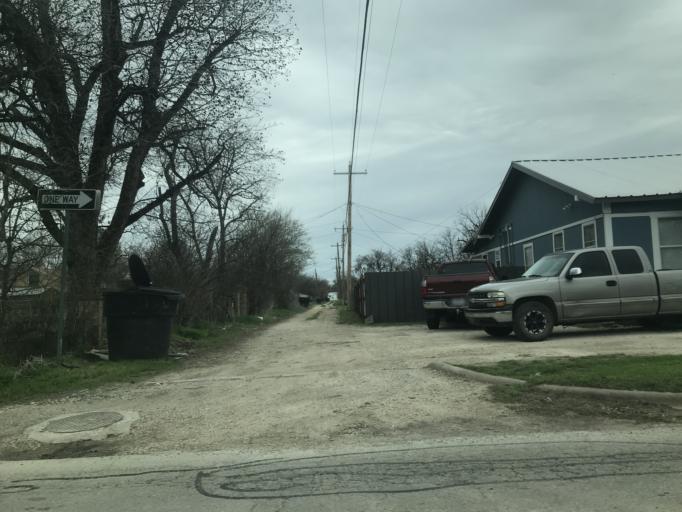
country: US
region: Texas
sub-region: Taylor County
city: Abilene
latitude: 32.4606
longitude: -99.7449
